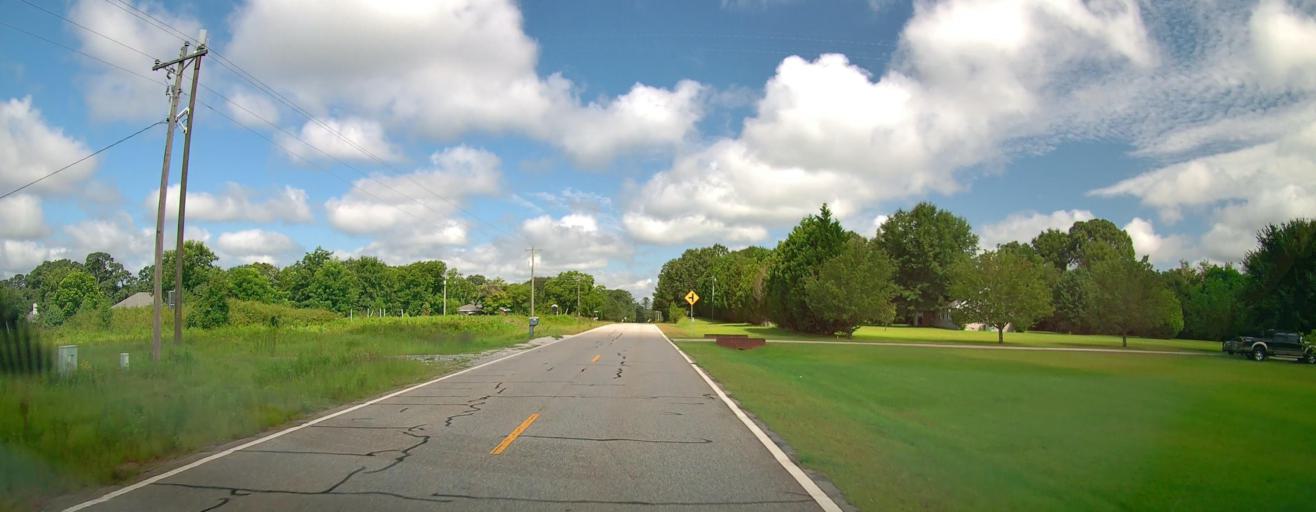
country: US
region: Georgia
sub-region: Peach County
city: Byron
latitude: 32.5982
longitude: -83.7828
